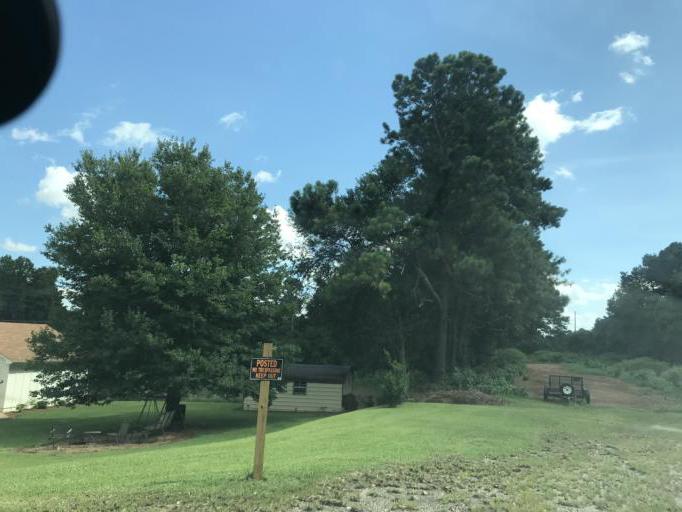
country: US
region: Georgia
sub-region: Forsyth County
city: Cumming
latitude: 34.2273
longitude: -84.2436
